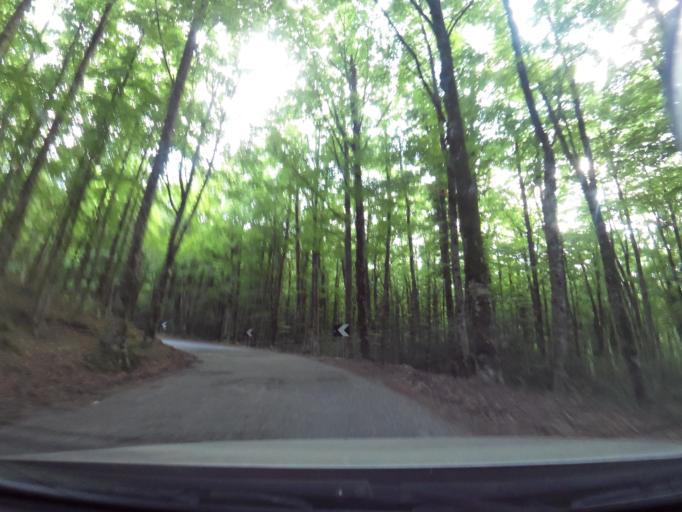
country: IT
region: Calabria
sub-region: Provincia di Vibo-Valentia
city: Nardodipace
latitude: 38.5042
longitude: 16.3798
